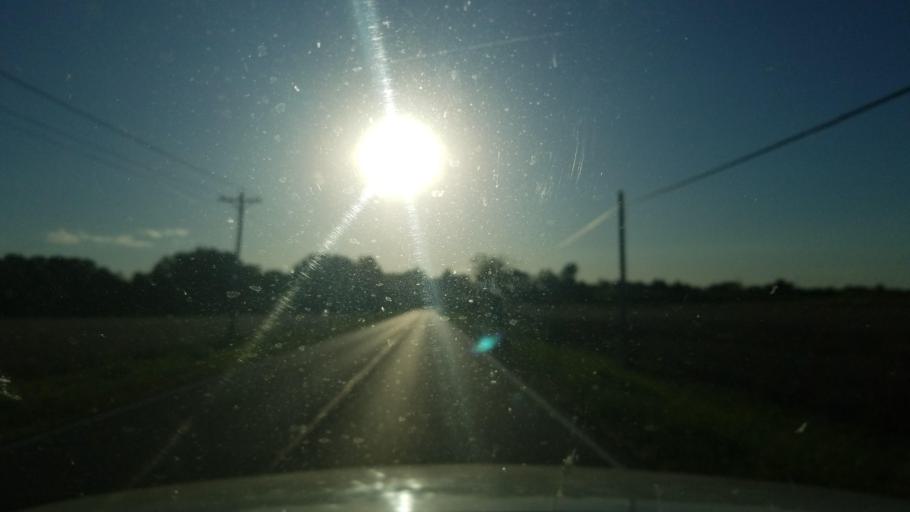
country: US
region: Illinois
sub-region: Saline County
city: Harrisburg
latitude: 37.6364
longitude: -88.5140
